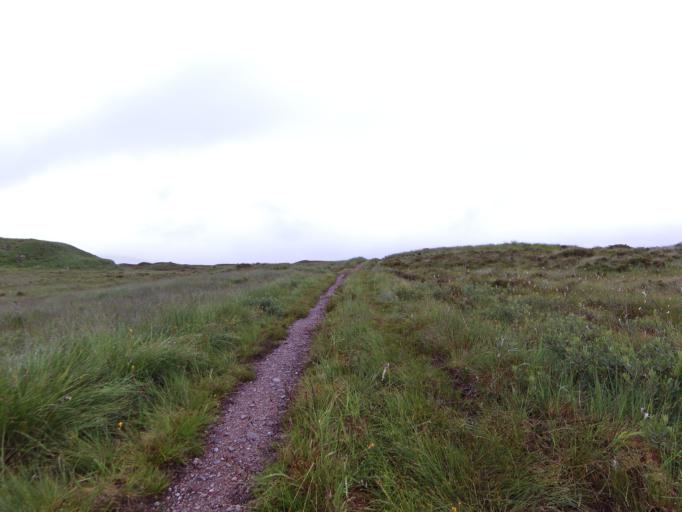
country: GB
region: Scotland
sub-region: Highland
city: Spean Bridge
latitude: 56.7681
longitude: -4.7041
